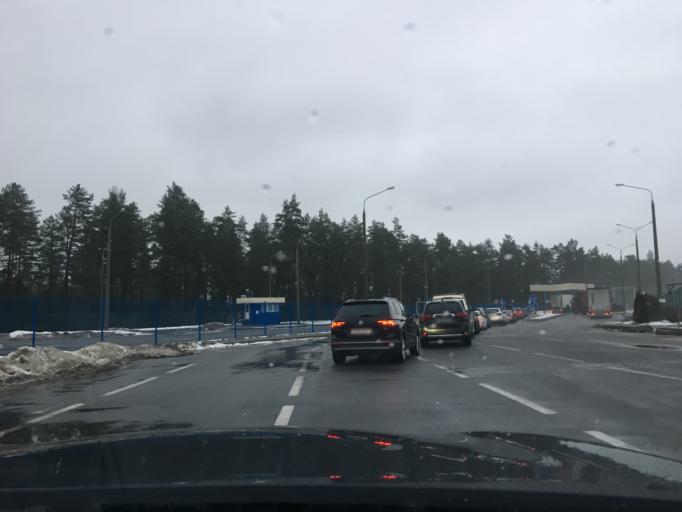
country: LT
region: Alytaus apskritis
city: Druskininkai
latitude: 53.9403
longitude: 23.9669
